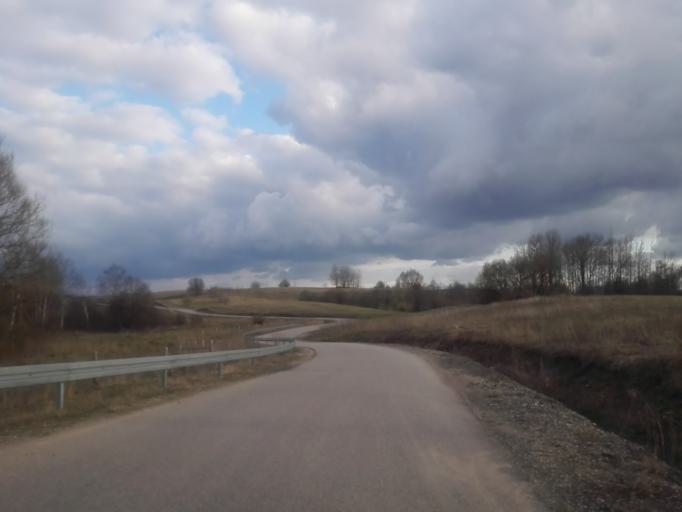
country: PL
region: Podlasie
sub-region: Suwalki
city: Suwalki
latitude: 54.2055
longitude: 22.9819
